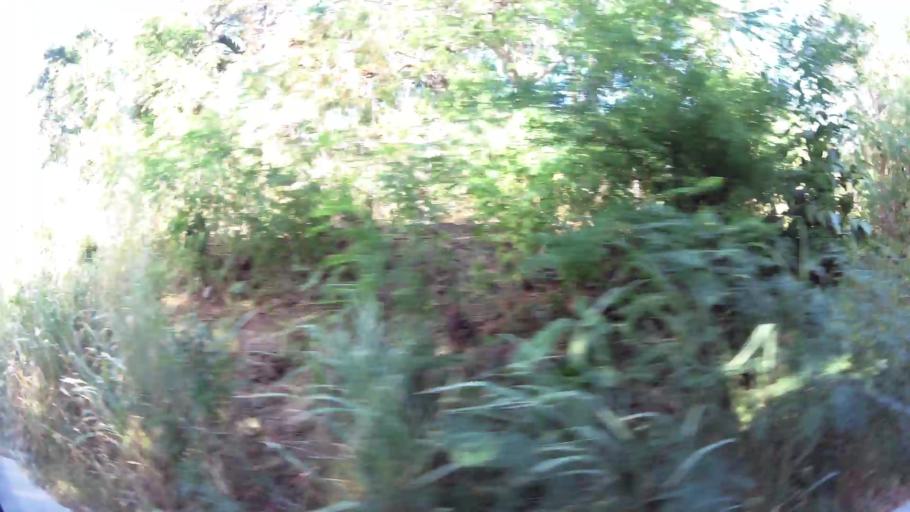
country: LC
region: Gros-Islet
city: Gros Islet
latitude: 14.1038
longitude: -60.9403
